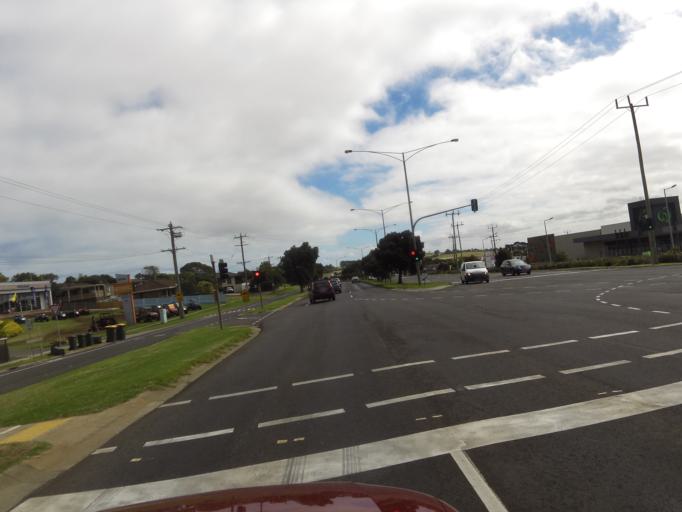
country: AU
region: Victoria
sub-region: Warrnambool
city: Warrnambool
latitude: -38.3834
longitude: 142.5195
